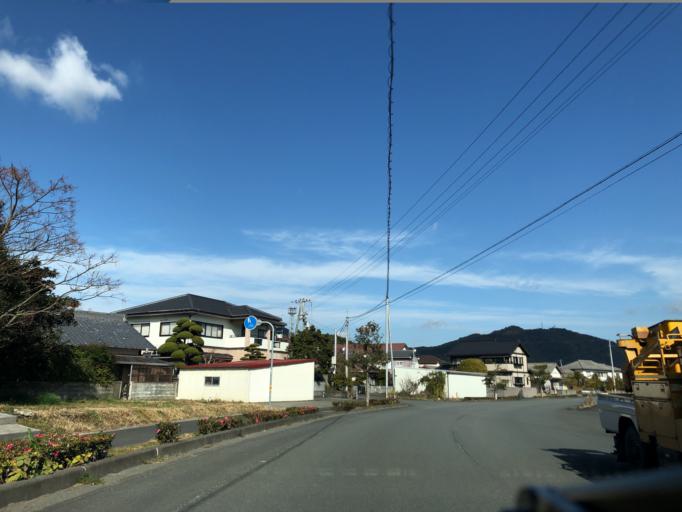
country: JP
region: Kochi
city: Sukumo
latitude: 32.9219
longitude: 132.7016
